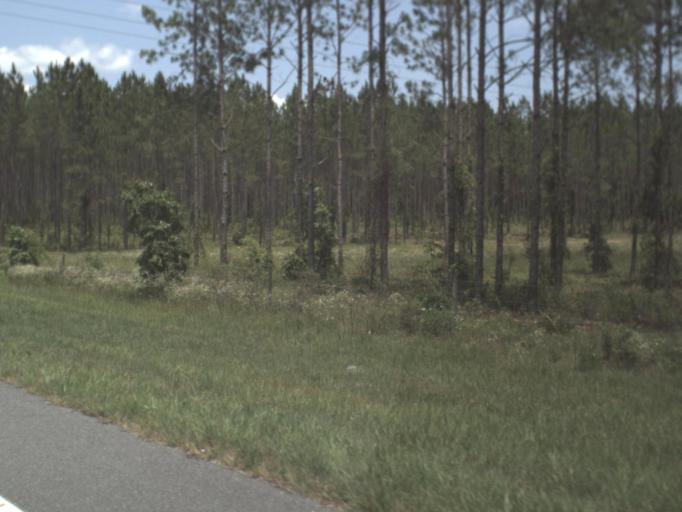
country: US
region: Florida
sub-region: Levy County
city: Williston
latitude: 29.4330
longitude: -82.4161
